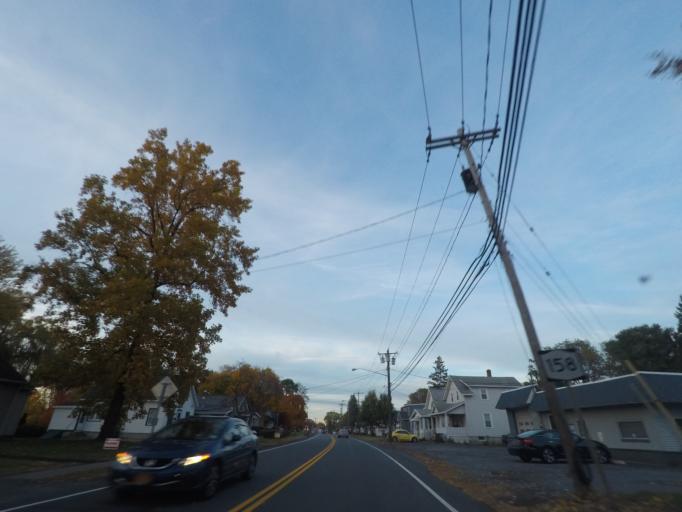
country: US
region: New York
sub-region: Schenectady County
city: Rotterdam
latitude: 42.7820
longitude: -73.9710
